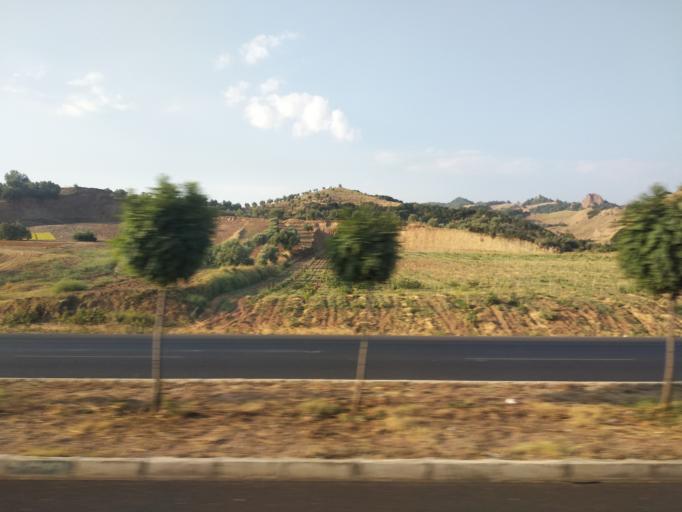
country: TR
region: Manisa
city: Ahmetli
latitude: 38.5102
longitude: 27.9754
